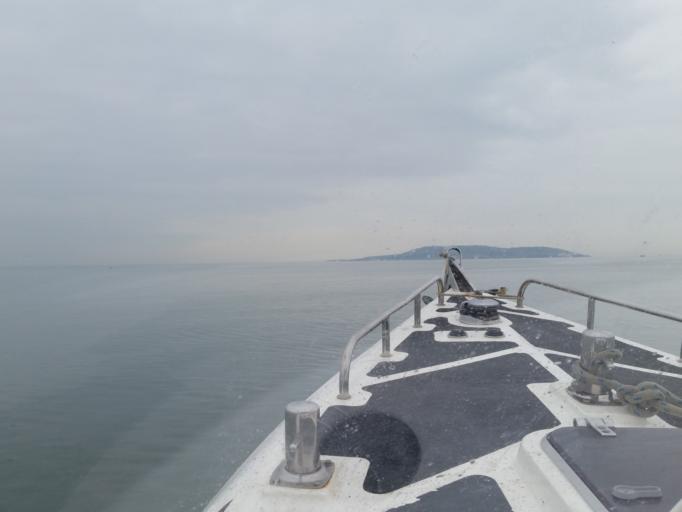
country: IE
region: Leinster
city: Portraine
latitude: 53.4613
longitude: -6.0986
